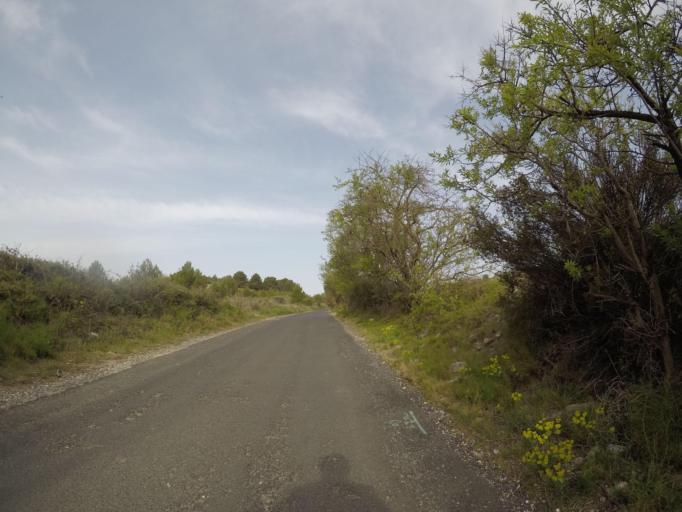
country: FR
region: Languedoc-Roussillon
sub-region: Departement des Pyrenees-Orientales
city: Baixas
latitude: 42.7690
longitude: 2.8083
